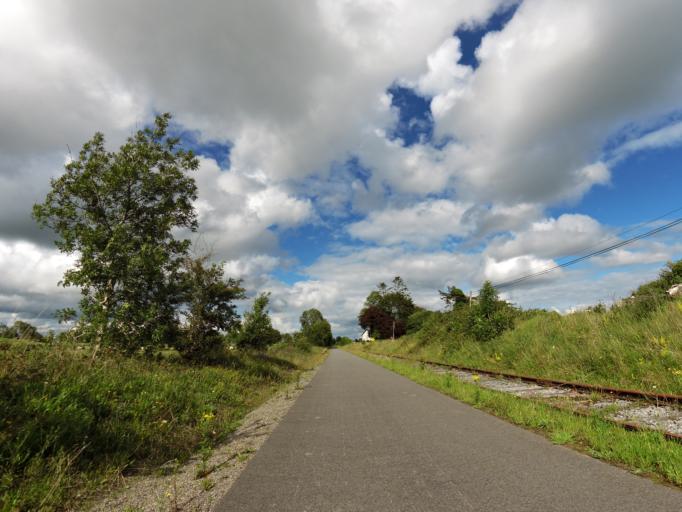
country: IE
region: Leinster
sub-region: An Iarmhi
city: Kilbeggan
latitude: 53.4488
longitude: -7.5337
